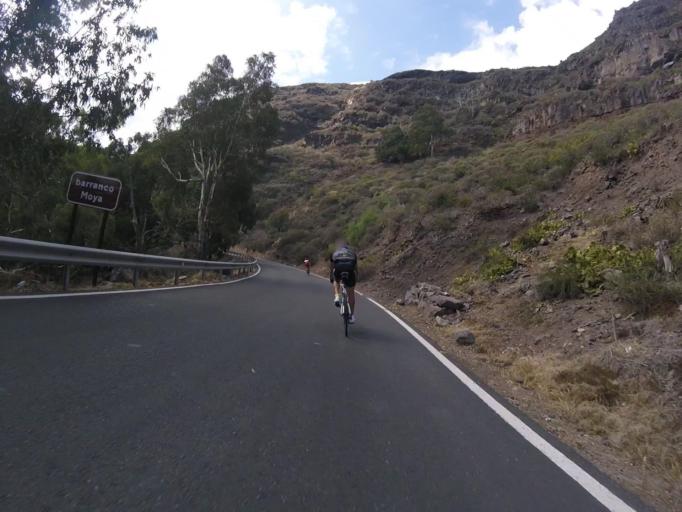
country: ES
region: Canary Islands
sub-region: Provincia de Las Palmas
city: Moya
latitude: 28.1386
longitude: -15.5920
